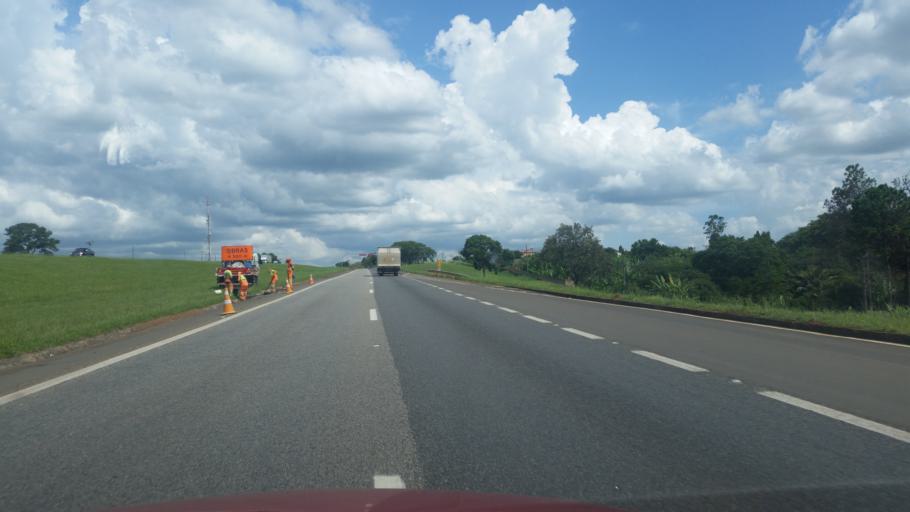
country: BR
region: Sao Paulo
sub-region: Tatui
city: Tatui
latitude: -23.2713
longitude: -47.8322
